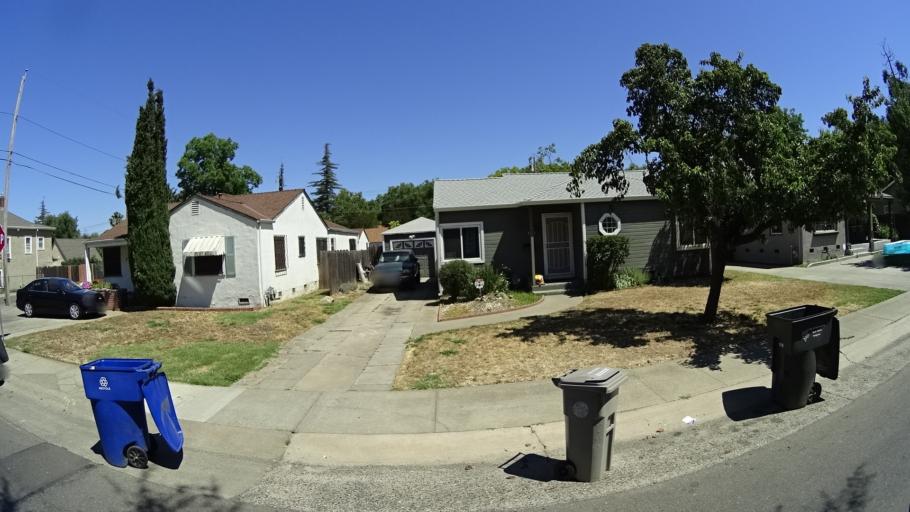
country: US
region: California
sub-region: Sacramento County
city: Parkway
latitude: 38.5412
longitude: -121.4576
